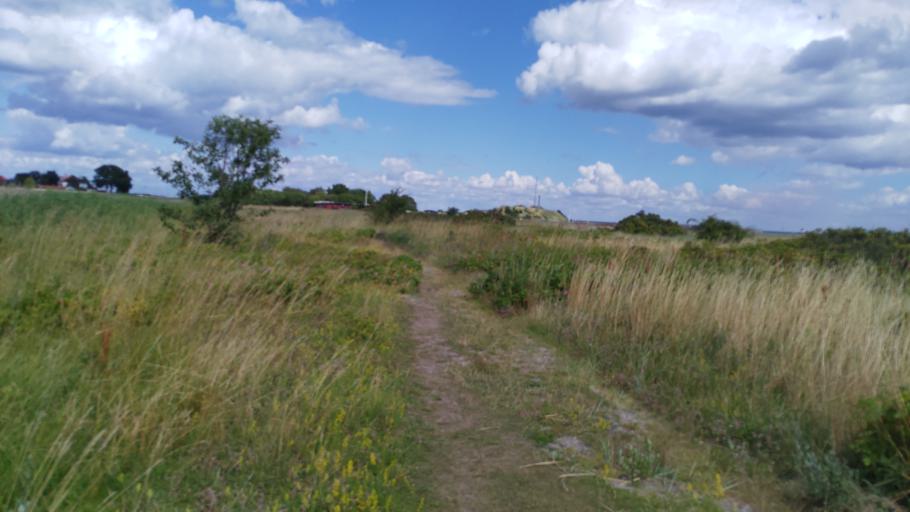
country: DK
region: Capital Region
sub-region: Dragor Kommune
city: Dragor
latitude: 55.5858
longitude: 12.6691
